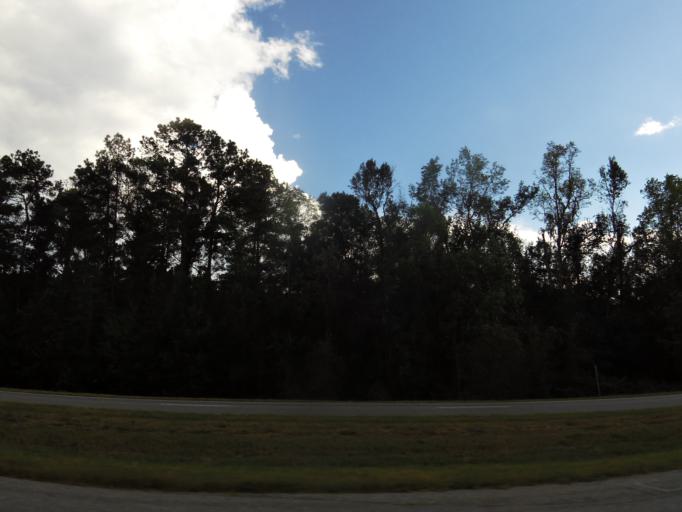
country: US
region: Georgia
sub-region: Brooks County
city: Quitman
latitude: 30.7923
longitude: -83.4693
